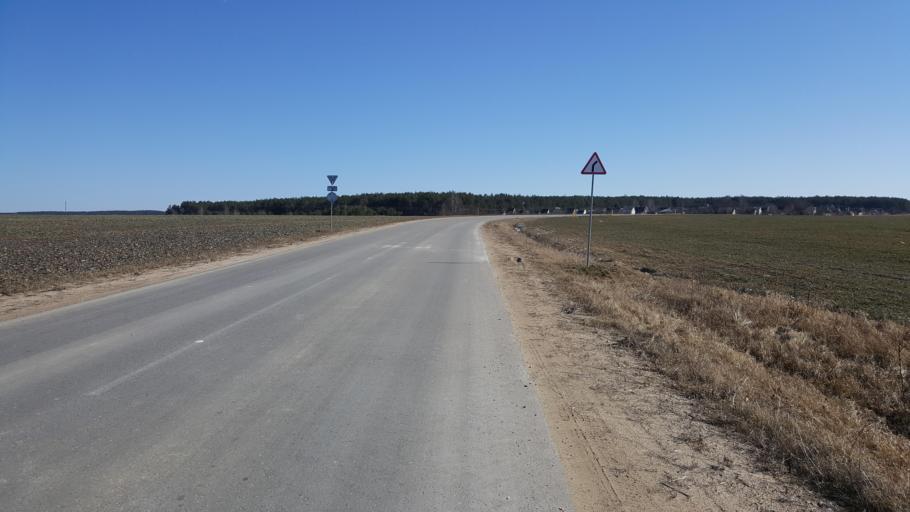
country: BY
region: Brest
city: Kamyanyets
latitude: 52.3704
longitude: 23.7953
